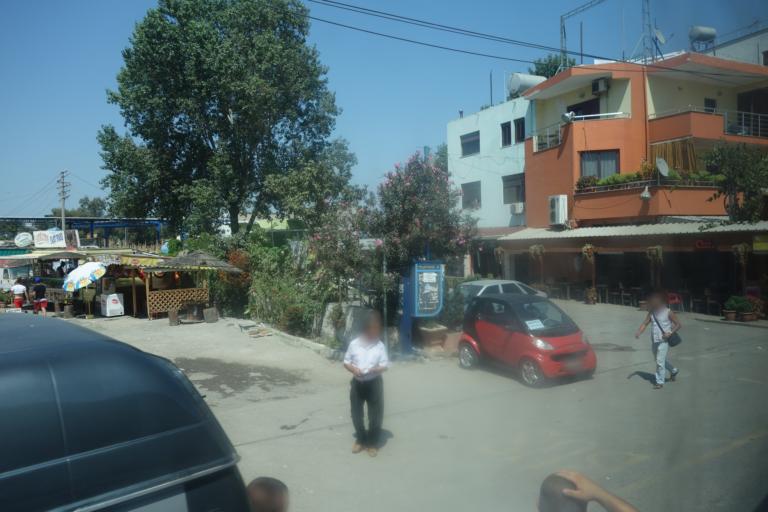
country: AL
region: Durres
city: Durres
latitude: 41.3163
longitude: 19.4705
